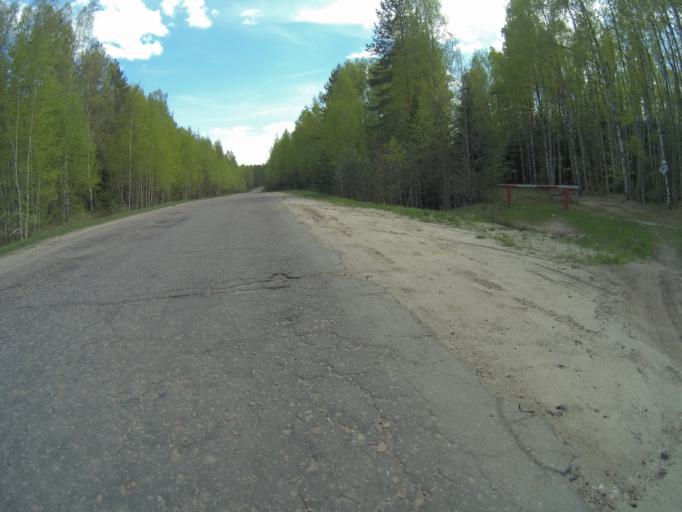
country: RU
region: Vladimir
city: Raduzhnyy
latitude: 55.9823
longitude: 40.2419
